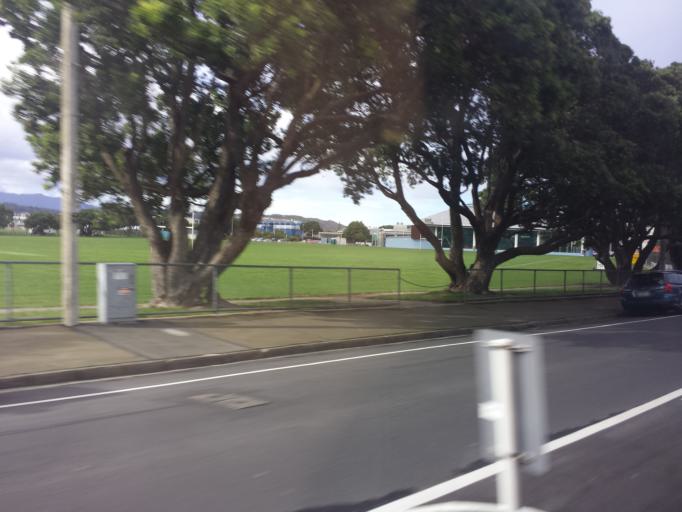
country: NZ
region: Wellington
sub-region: Wellington City
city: Wellington
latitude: -41.3132
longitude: 174.7931
